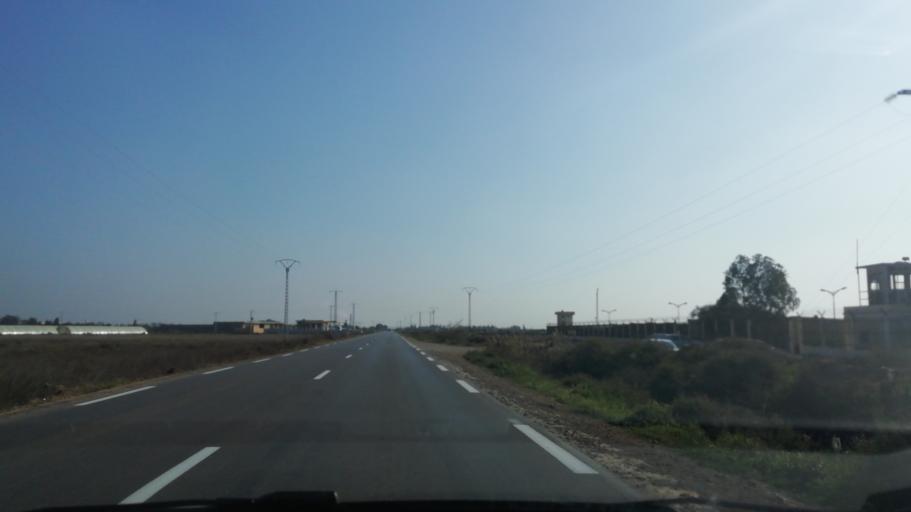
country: DZ
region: Mostaganem
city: Mostaganem
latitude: 35.7485
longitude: 0.0278
